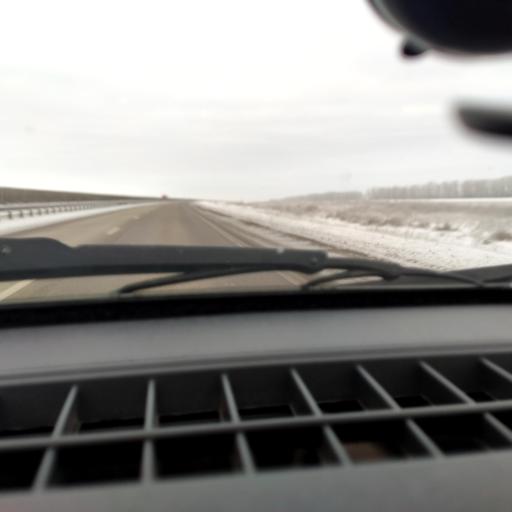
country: RU
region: Bashkortostan
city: Kushnarenkovo
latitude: 55.0858
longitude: 55.2581
